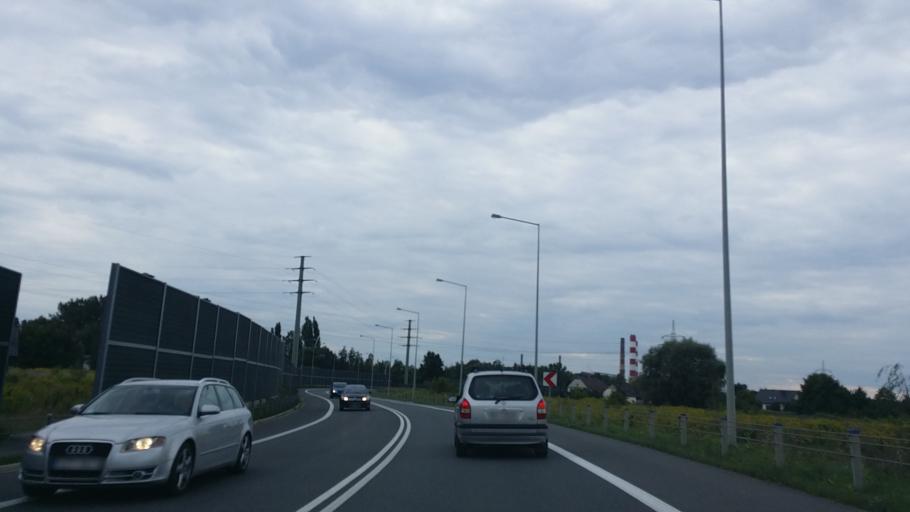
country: PL
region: Lesser Poland Voivodeship
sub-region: Powiat krakowski
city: Skawina
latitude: 49.9877
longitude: 19.8224
